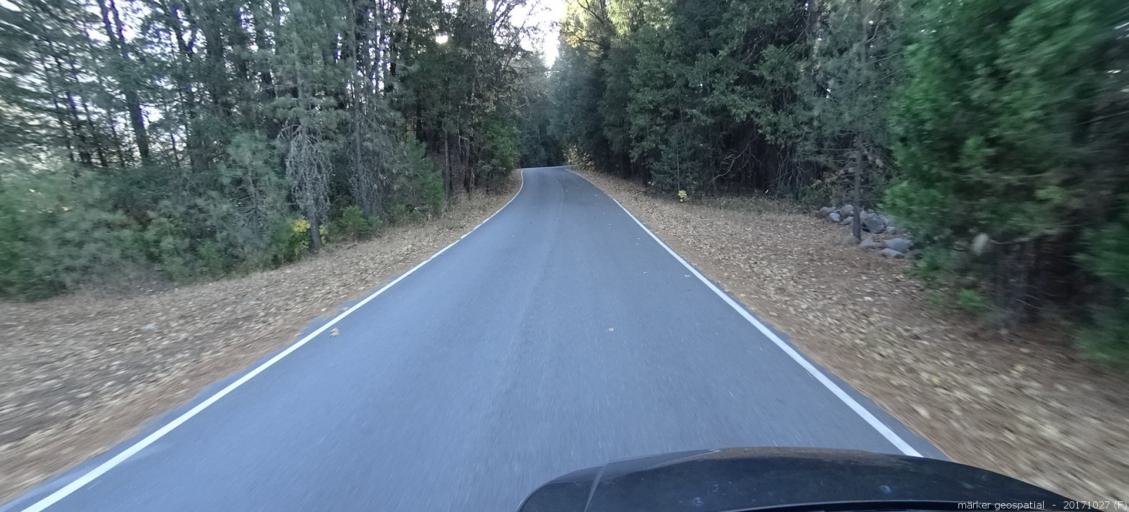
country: US
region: California
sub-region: Shasta County
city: Burney
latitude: 41.0004
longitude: -121.8871
